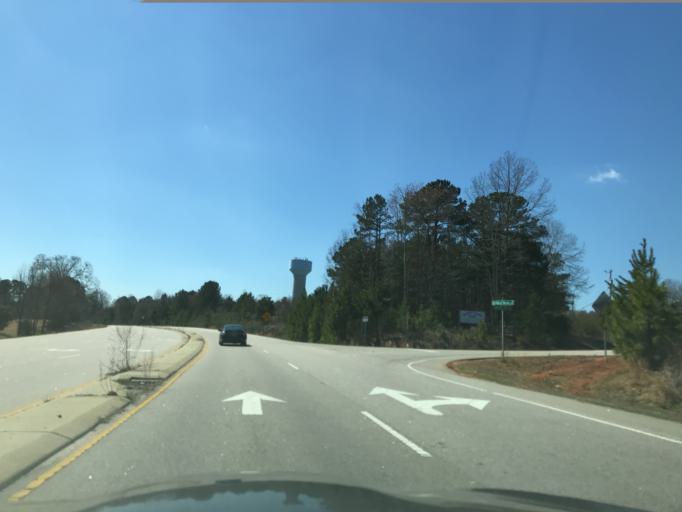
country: US
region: North Carolina
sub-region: Wake County
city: Wake Forest
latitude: 35.9702
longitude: -78.5581
